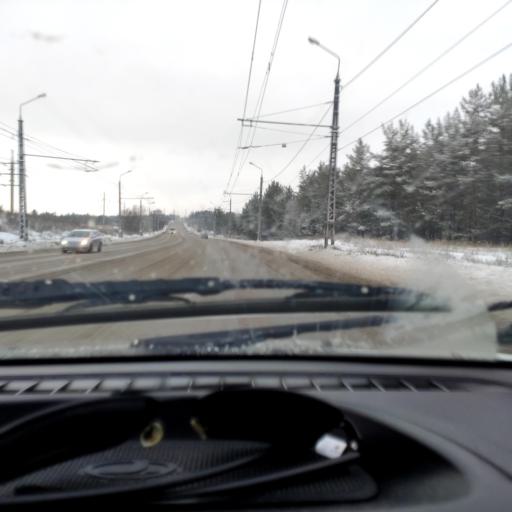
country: RU
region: Samara
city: Zhigulevsk
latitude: 53.5005
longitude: 49.5132
